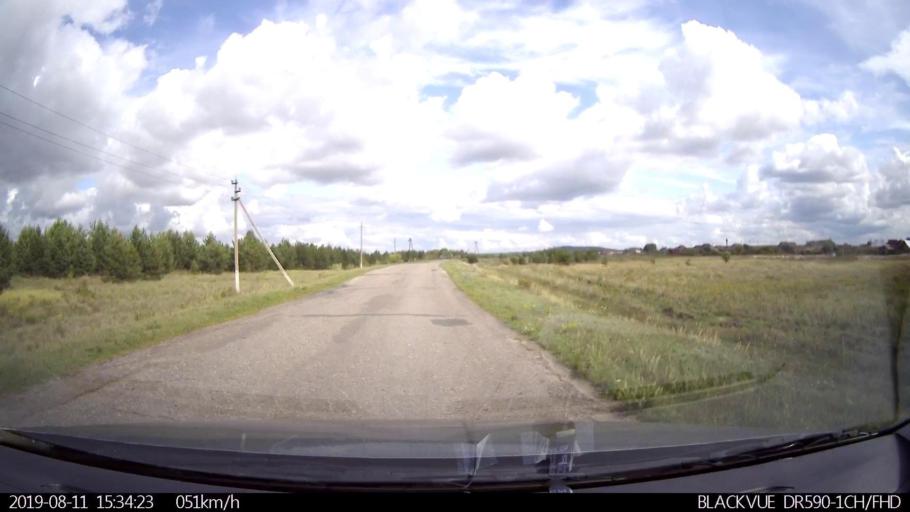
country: RU
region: Ulyanovsk
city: Ignatovka
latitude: 53.8617
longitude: 47.5949
